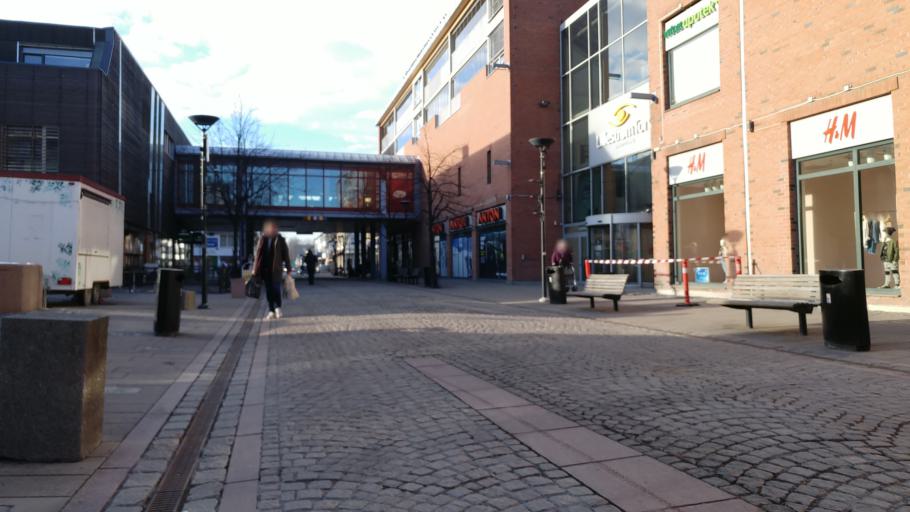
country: NO
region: Akershus
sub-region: Skedsmo
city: Lillestrom
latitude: 59.9563
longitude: 11.0502
